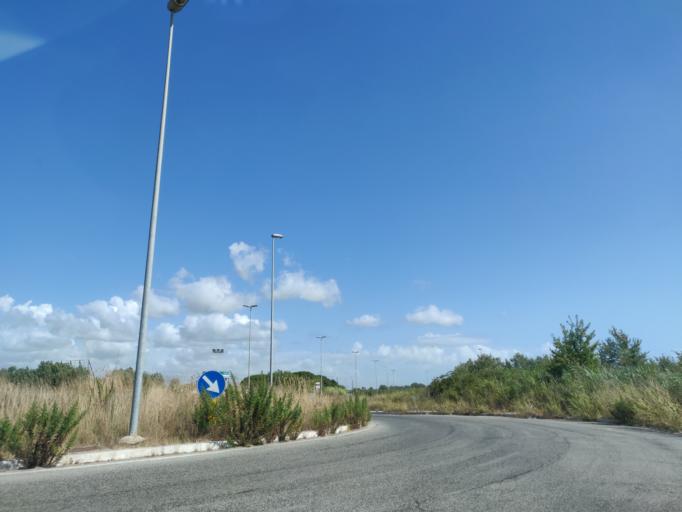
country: IT
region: Latium
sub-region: Citta metropolitana di Roma Capitale
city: Npp 23 (Parco Leonardo)
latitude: 41.7949
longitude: 12.2904
